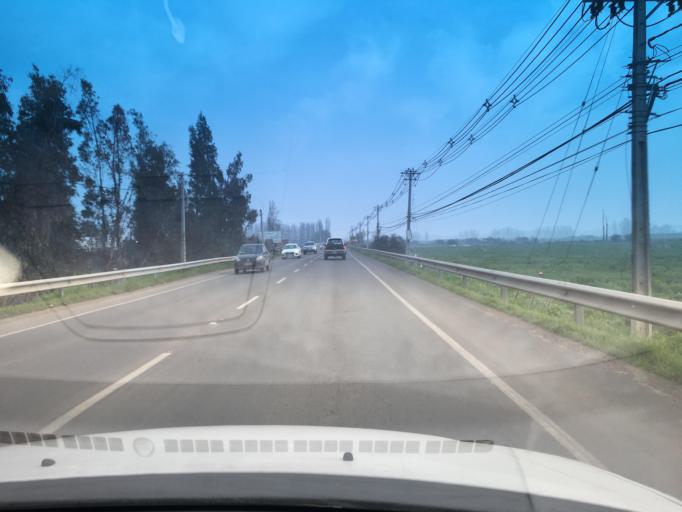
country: CL
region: Santiago Metropolitan
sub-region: Provincia de Chacabuco
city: Lampa
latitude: -33.3368
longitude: -70.8166
